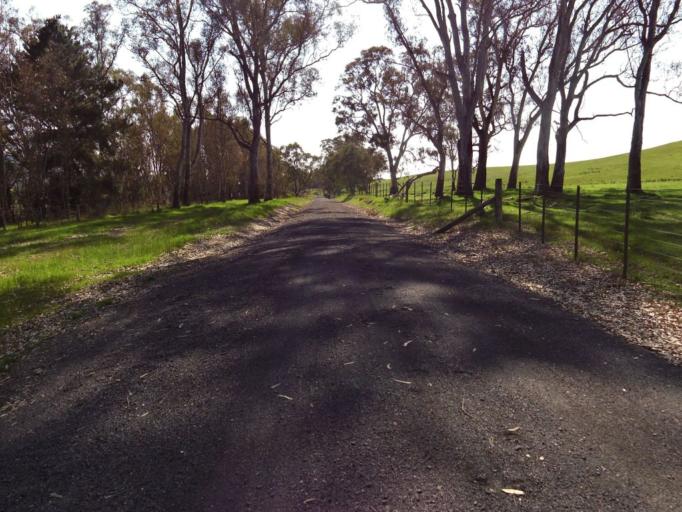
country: AU
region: Victoria
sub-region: Murrindindi
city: Alexandra
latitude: -37.1348
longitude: 145.5923
